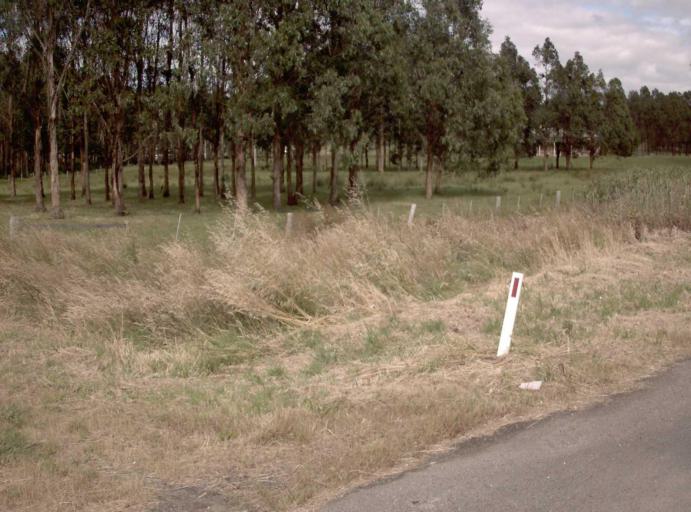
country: AU
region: Victoria
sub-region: Latrobe
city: Morwell
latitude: -38.2021
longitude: 146.4414
